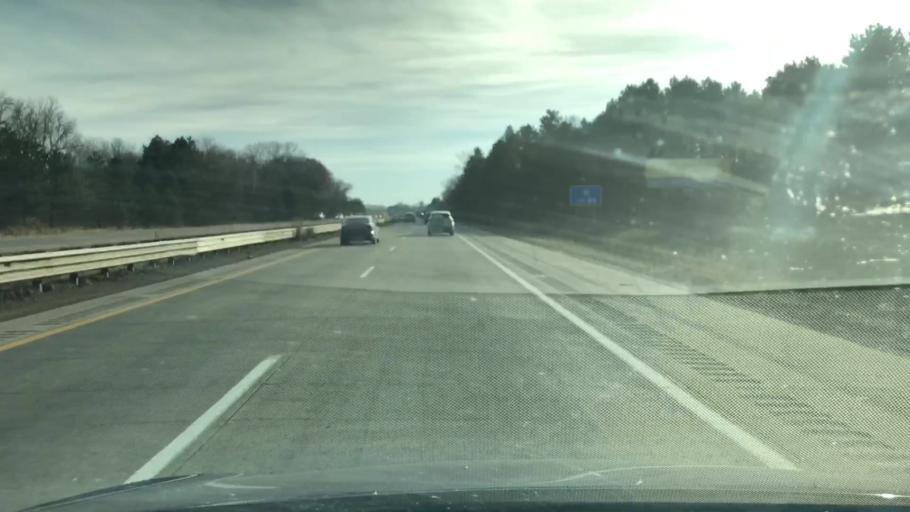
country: US
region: Michigan
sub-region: Genesee County
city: Lake Fenton
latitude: 42.9264
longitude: -83.7254
